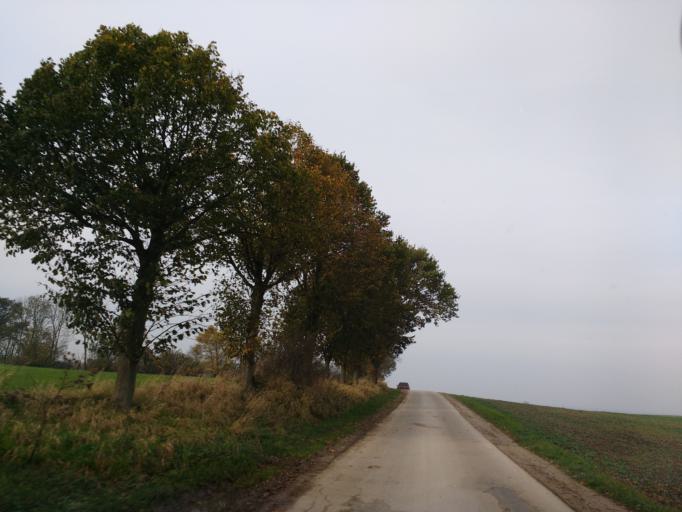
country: DE
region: Mecklenburg-Vorpommern
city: Klutz
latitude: 54.0042
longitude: 11.1607
